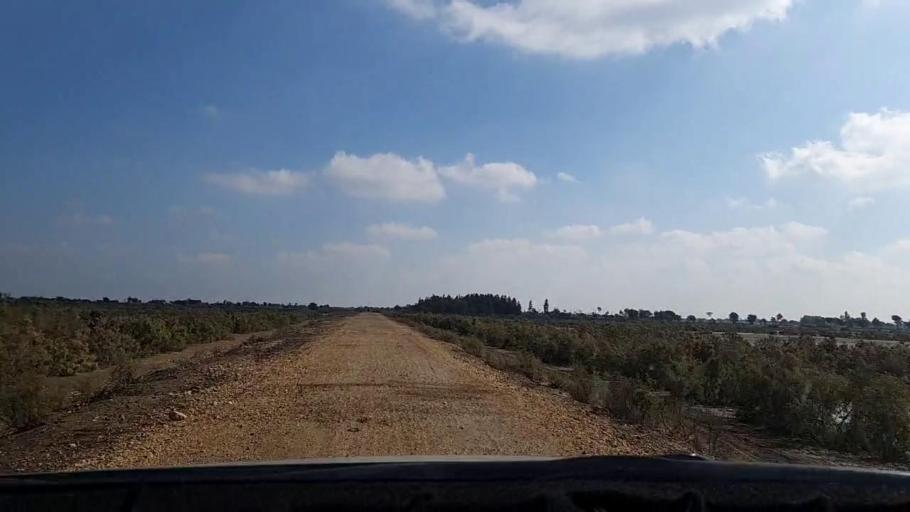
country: PK
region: Sindh
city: Pithoro
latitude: 25.7322
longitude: 69.2837
